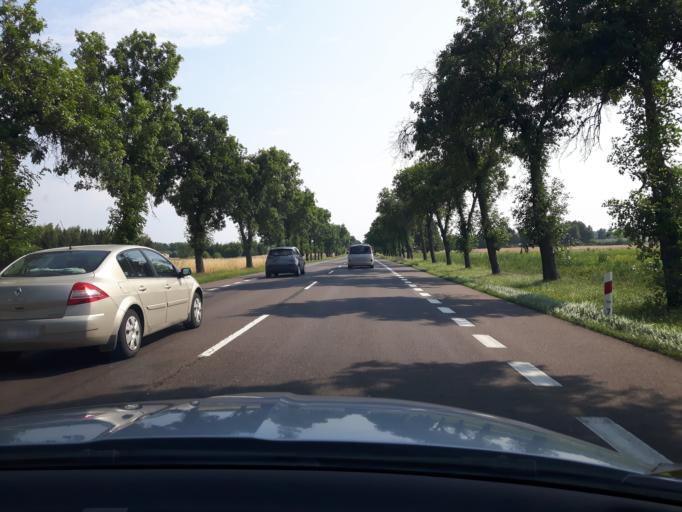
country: PL
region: Masovian Voivodeship
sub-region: Powiat mlawski
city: Strzegowo
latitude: 52.8697
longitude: 20.2927
